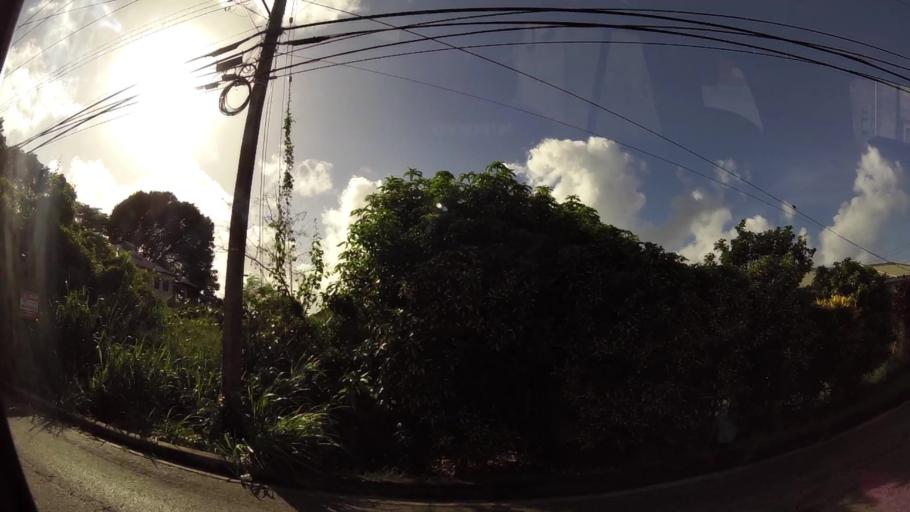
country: BB
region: Saint James
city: Holetown
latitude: 13.1543
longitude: -59.6104
